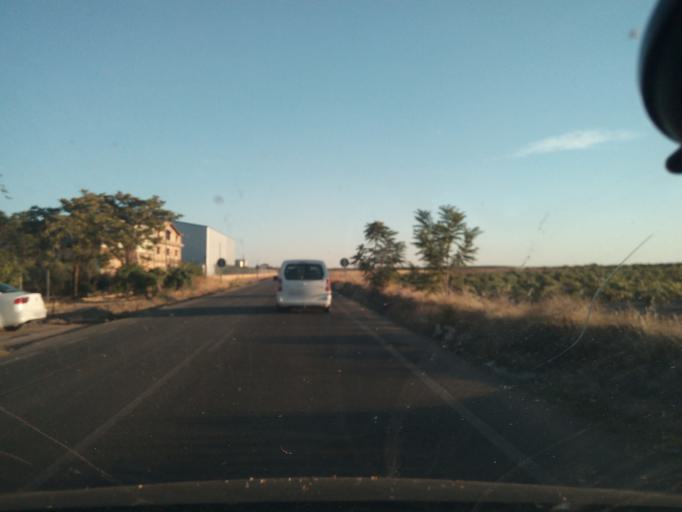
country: ES
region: Castille-La Mancha
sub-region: Province of Toledo
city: Villacanas
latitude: 39.6080
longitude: -3.3389
